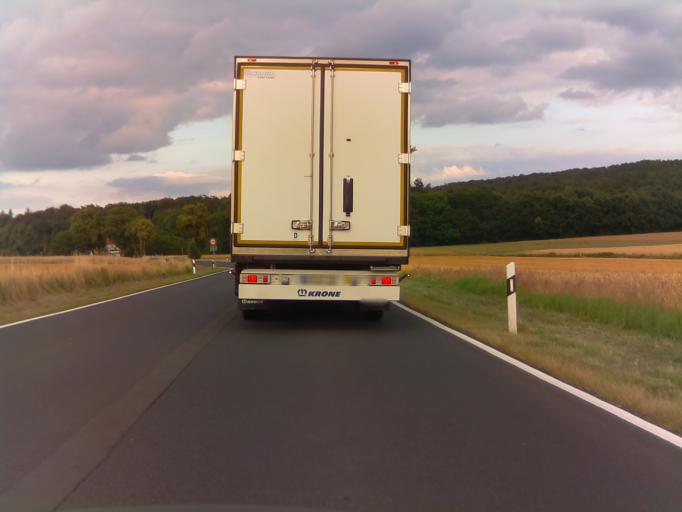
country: DE
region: Hesse
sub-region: Regierungsbezirk Giessen
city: Alsfeld
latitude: 50.7477
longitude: 9.3088
